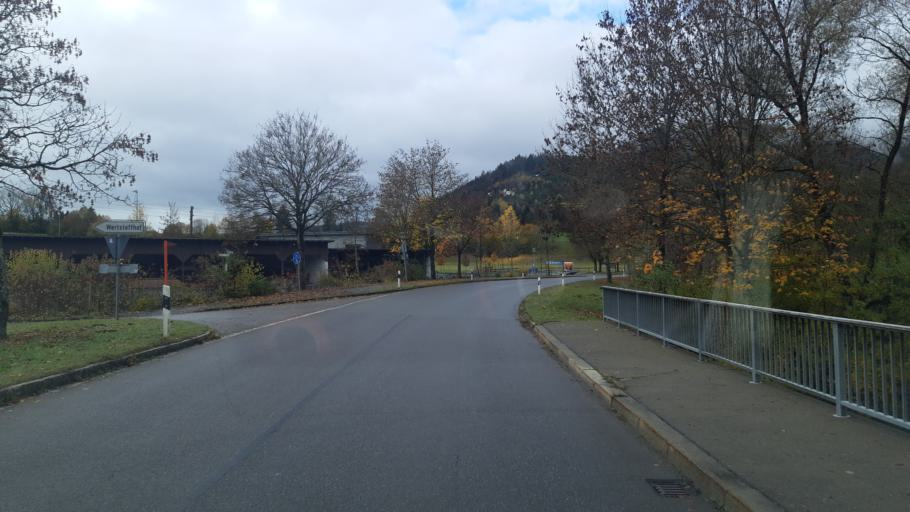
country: DE
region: Bavaria
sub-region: Swabia
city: Weitnau
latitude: 47.6411
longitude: 10.0985
